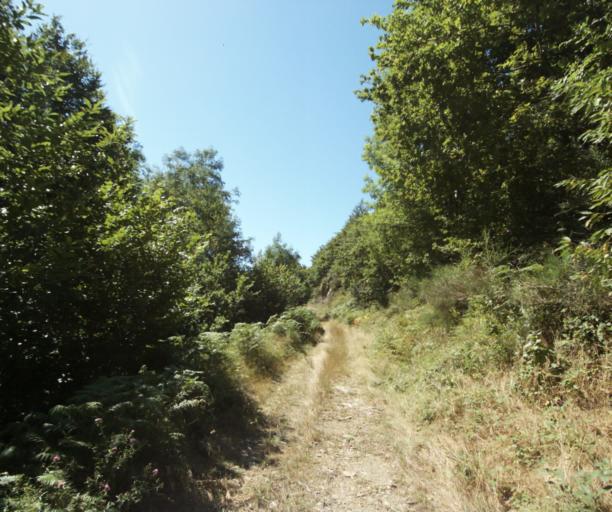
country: FR
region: Midi-Pyrenees
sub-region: Departement du Tarn
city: Soreze
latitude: 43.4389
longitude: 2.1031
